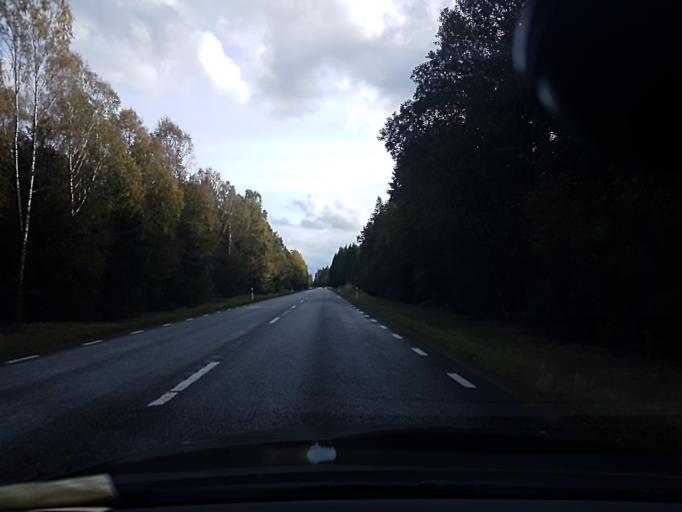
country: SE
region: Joenkoeping
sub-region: Varnamo Kommun
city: Bredaryd
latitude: 57.1952
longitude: 13.7186
